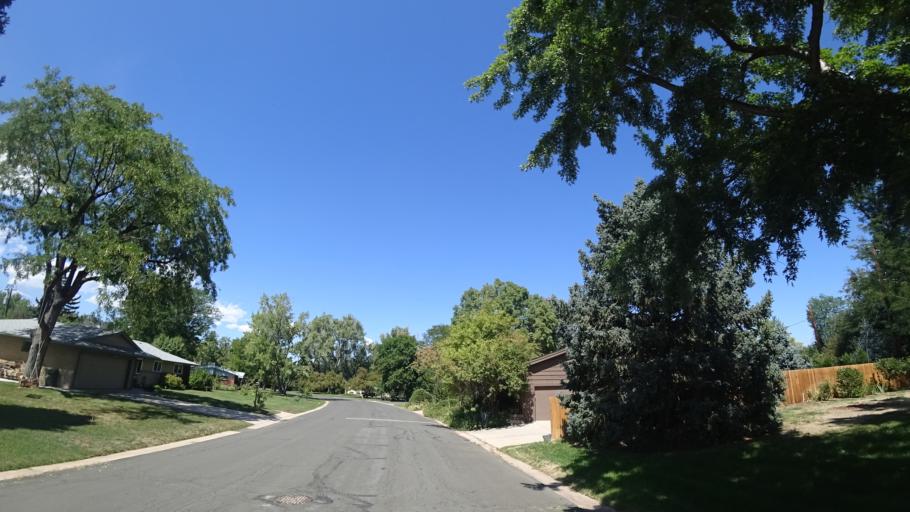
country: US
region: Colorado
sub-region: Arapahoe County
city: Littleton
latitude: 39.6074
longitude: -104.9958
